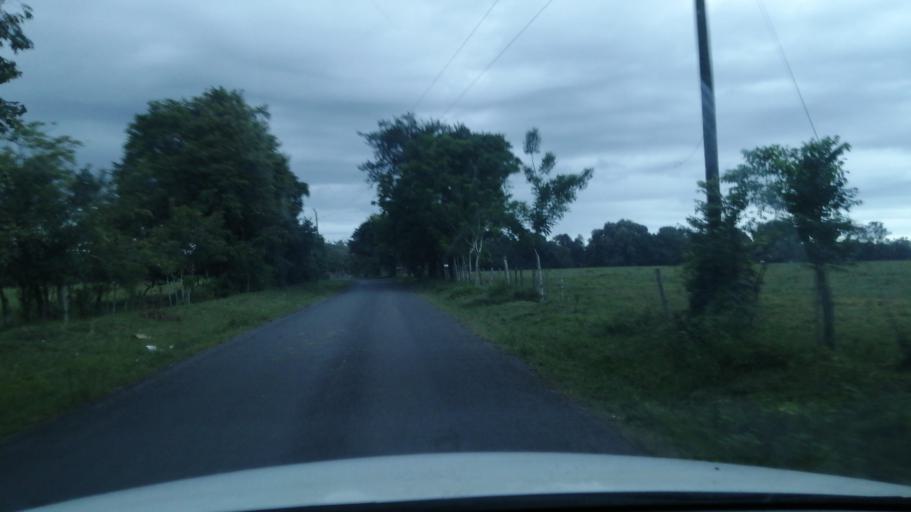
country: PA
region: Chiriqui
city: Alanje
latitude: 8.4051
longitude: -82.5005
